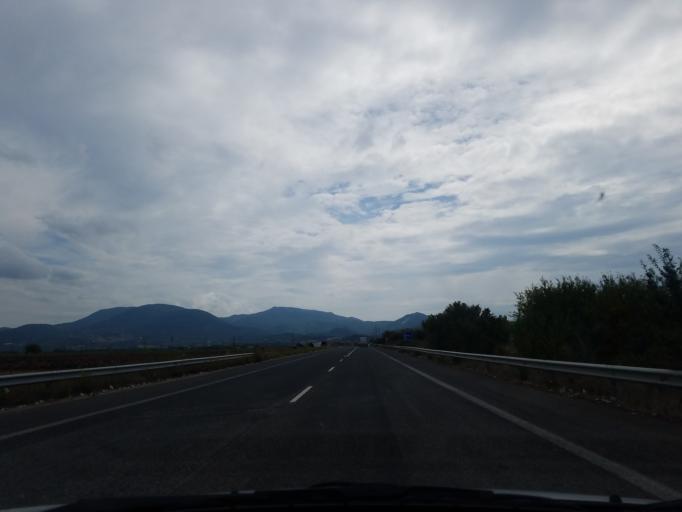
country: GR
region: Central Greece
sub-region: Nomos Fthiotidos
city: Domokos
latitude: 39.0458
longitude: 22.3488
